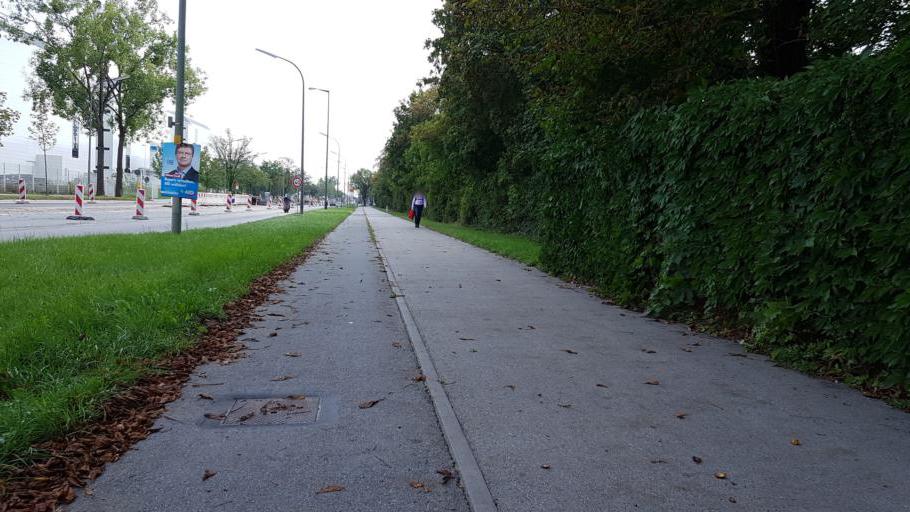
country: DE
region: Bavaria
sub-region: Upper Bavaria
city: Oberschleissheim
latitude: 48.1972
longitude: 11.5645
